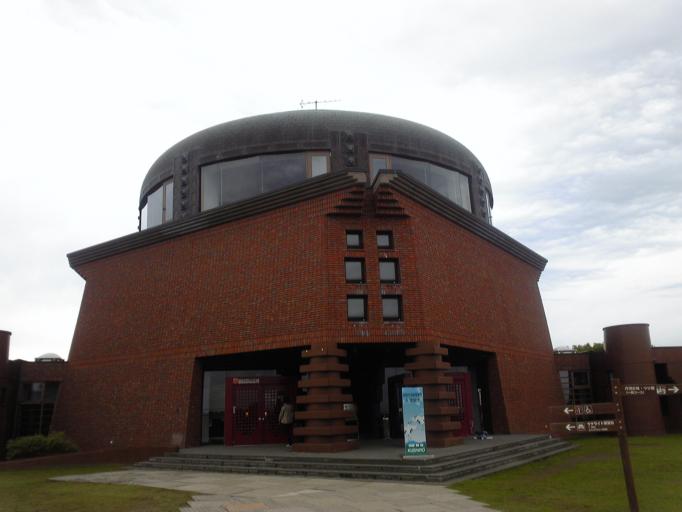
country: JP
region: Hokkaido
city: Kushiro
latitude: 43.0800
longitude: 144.3211
